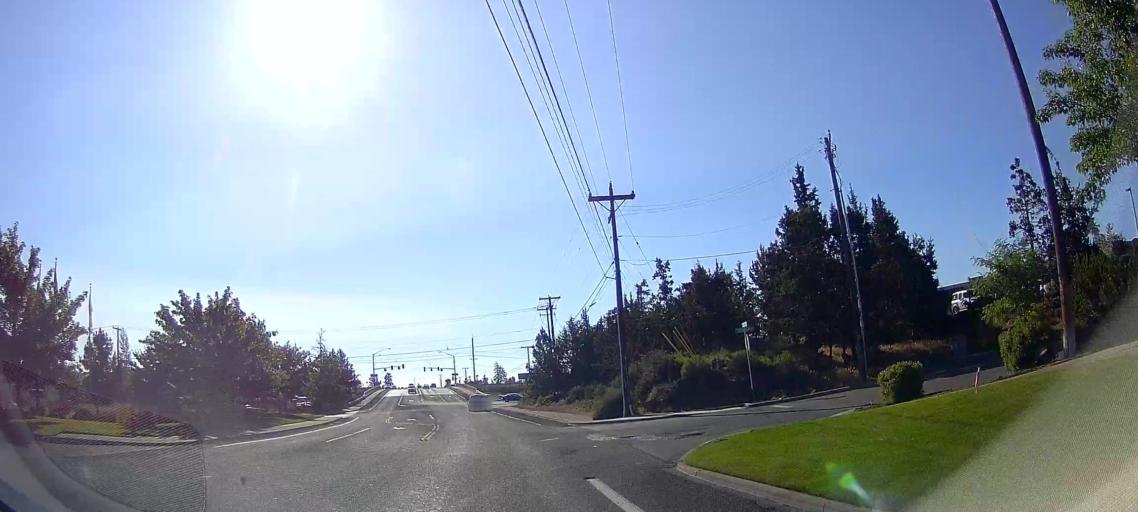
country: US
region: Oregon
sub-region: Deschutes County
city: Bend
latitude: 44.0913
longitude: -121.3035
